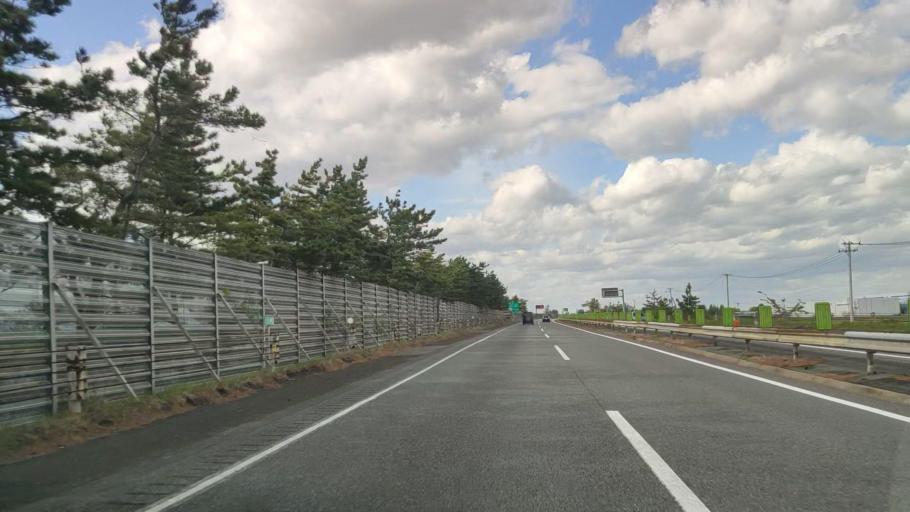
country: JP
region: Miyagi
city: Furukawa
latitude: 38.5838
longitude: 140.9297
